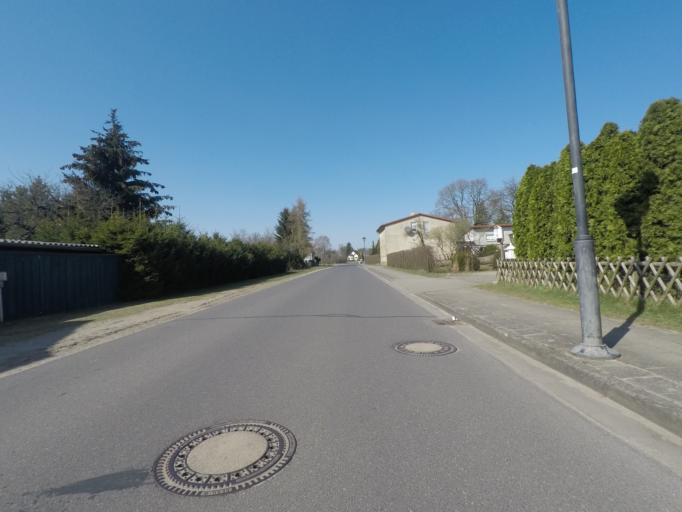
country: DE
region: Brandenburg
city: Melchow
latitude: 52.8540
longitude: 13.6816
